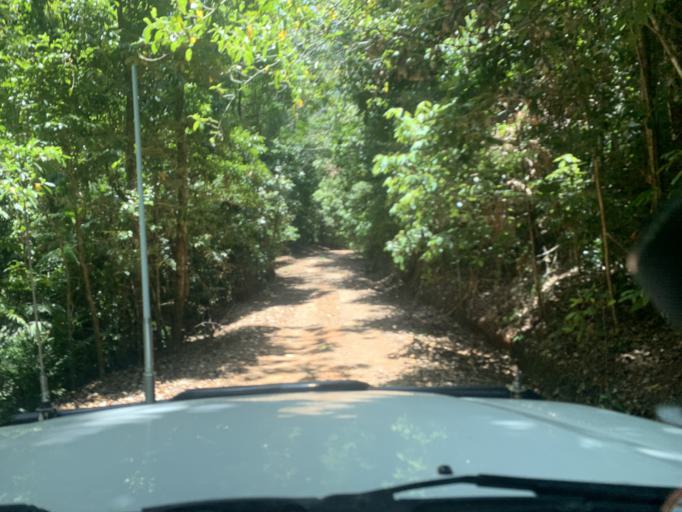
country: AU
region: Queensland
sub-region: Cairns
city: Woree
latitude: -16.9740
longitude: 145.6504
